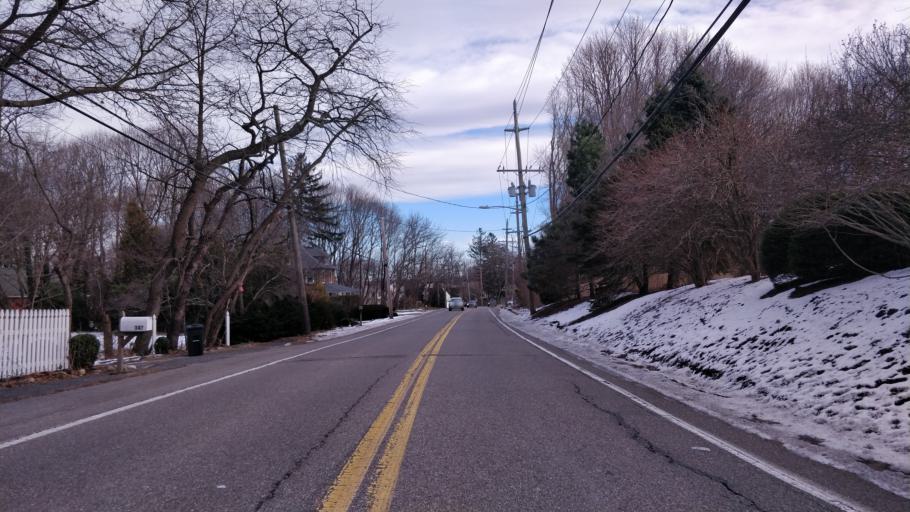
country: US
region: New York
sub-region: Suffolk County
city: Greenlawn
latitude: 40.8674
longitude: -73.3750
